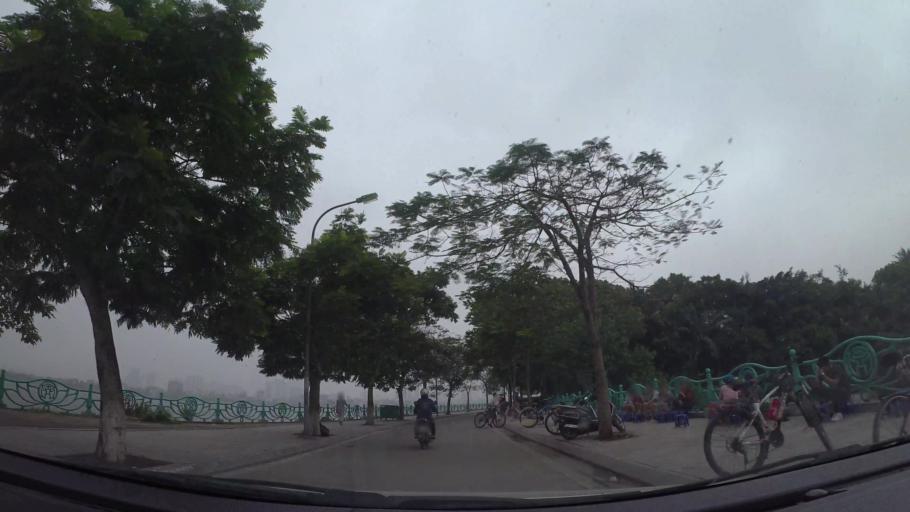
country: VN
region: Ha Noi
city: Tay Ho
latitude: 21.0592
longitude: 105.8188
